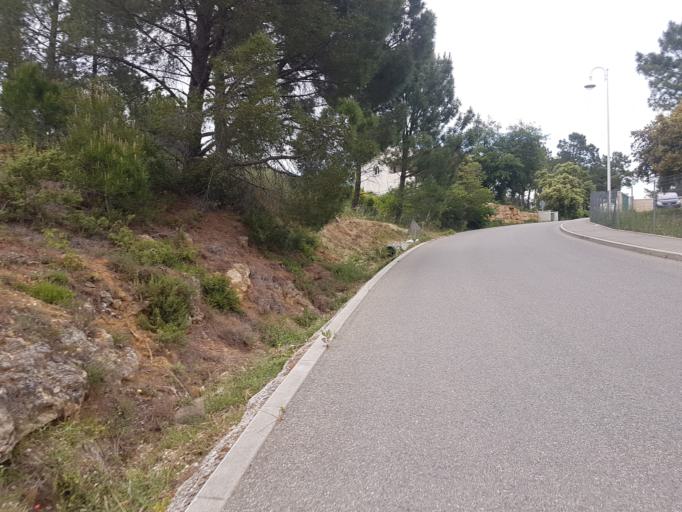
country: FR
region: Provence-Alpes-Cote d'Azur
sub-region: Departement du Vaucluse
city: Mondragon
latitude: 44.2416
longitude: 4.7189
